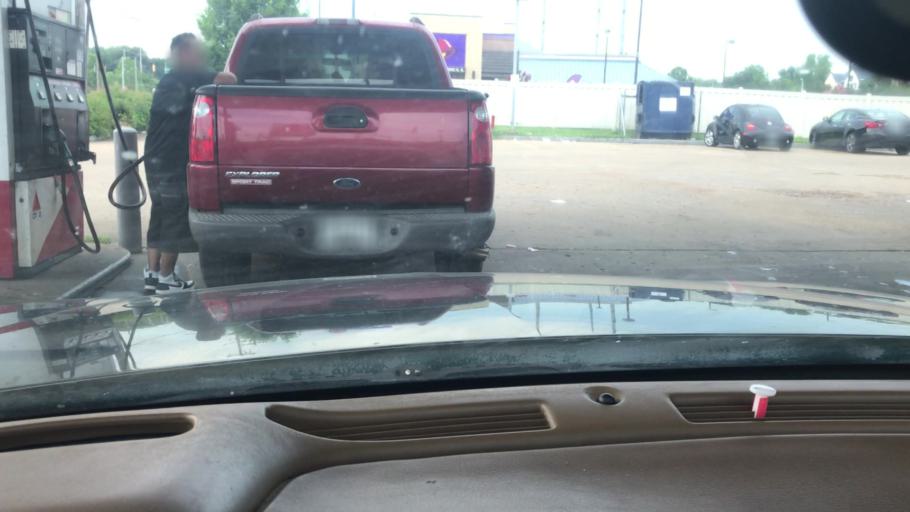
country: US
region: Tennessee
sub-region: Shelby County
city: Germantown
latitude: 35.0744
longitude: -89.9058
